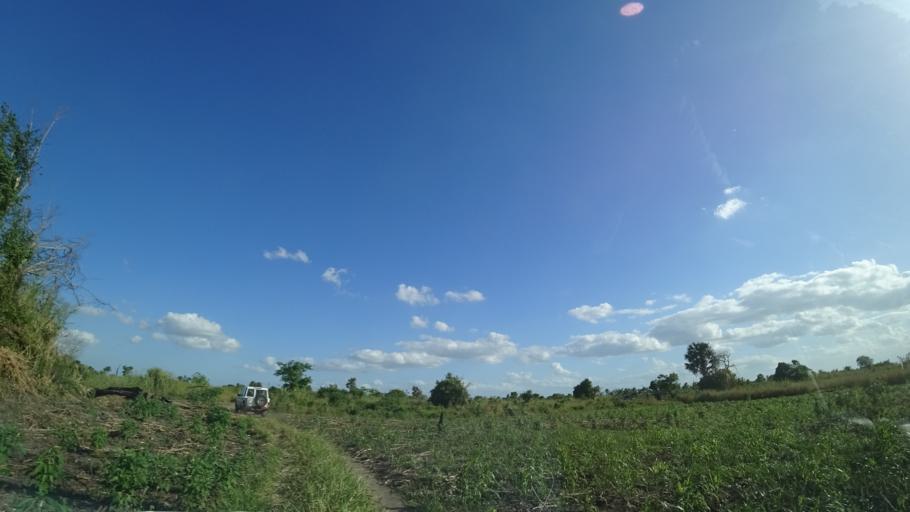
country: MZ
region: Sofala
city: Dondo
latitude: -19.3554
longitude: 34.5895
